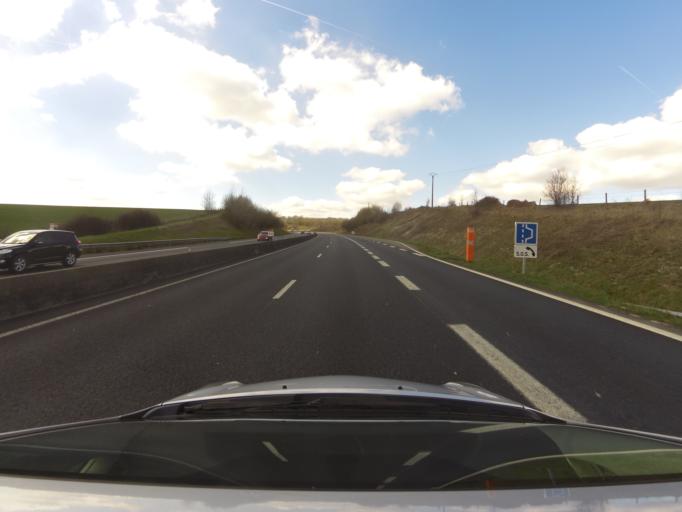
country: FR
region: Haute-Normandie
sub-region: Departement de la Seine-Maritime
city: Mesnieres-en-Bray
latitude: 49.7126
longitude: 1.3884
